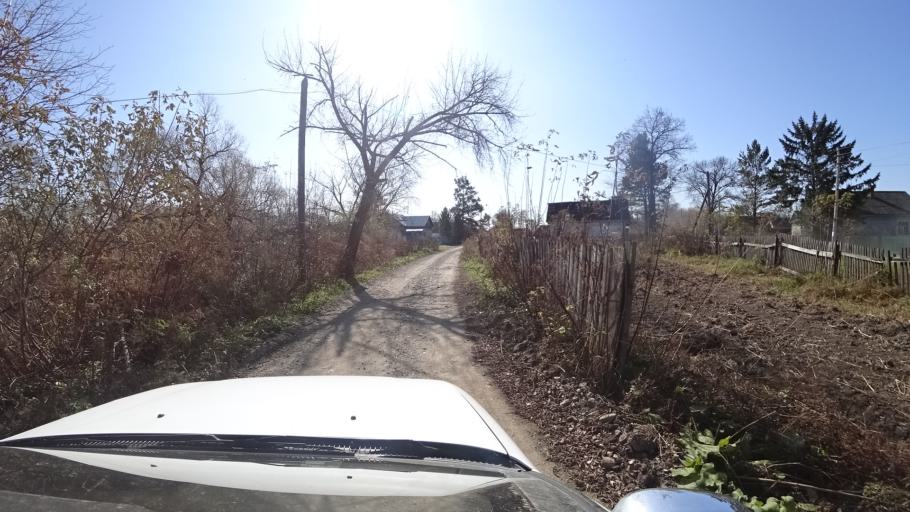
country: RU
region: Primorskiy
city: Dal'nerechensk
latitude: 45.9098
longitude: 133.7954
